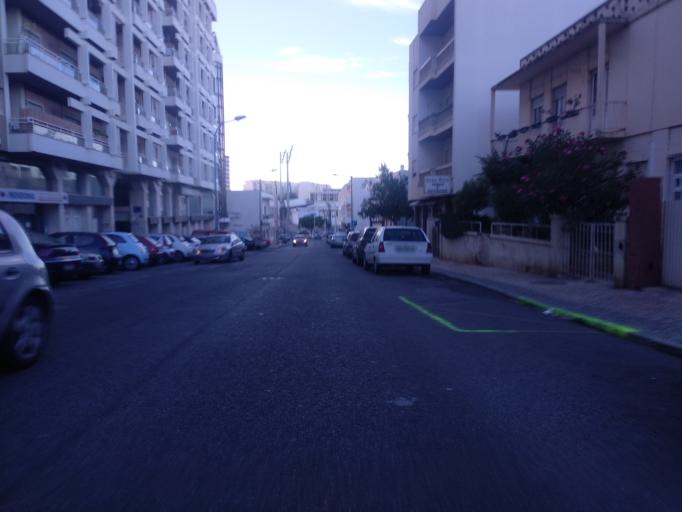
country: PT
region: Faro
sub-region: Faro
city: Faro
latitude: 37.0206
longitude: -7.9269
